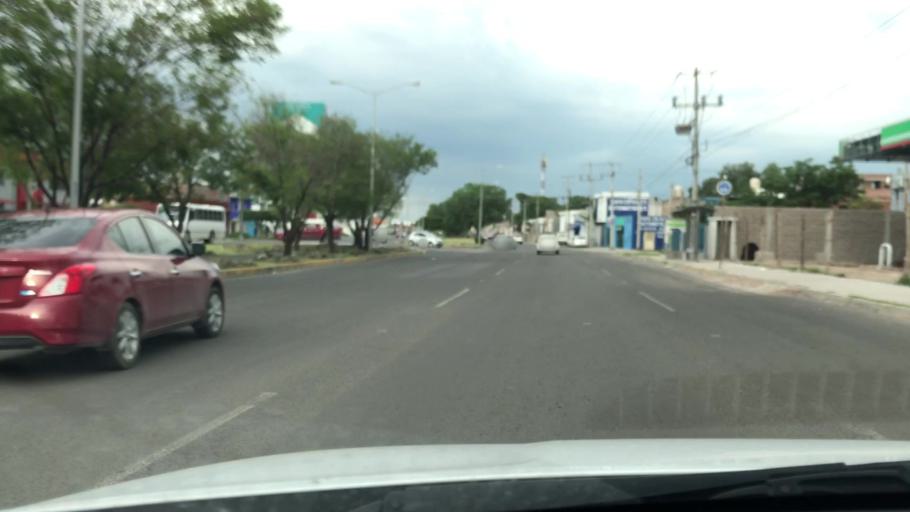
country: MX
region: Guanajuato
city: Celaya
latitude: 20.5364
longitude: -100.7973
